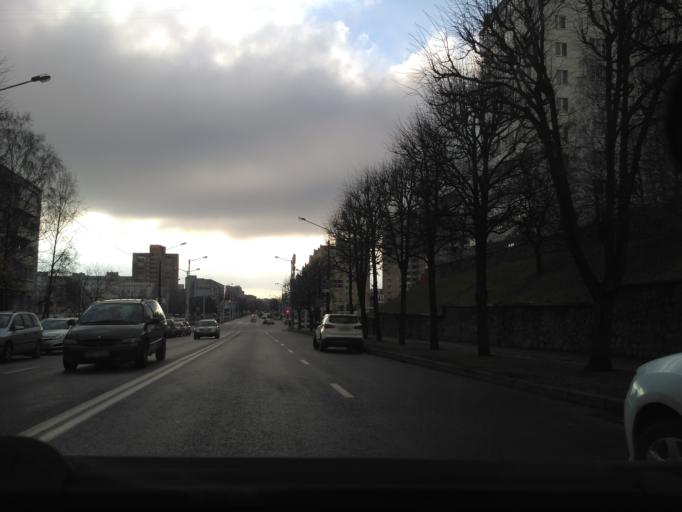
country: BY
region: Minsk
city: Novoye Medvezhino
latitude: 53.9100
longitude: 27.4808
